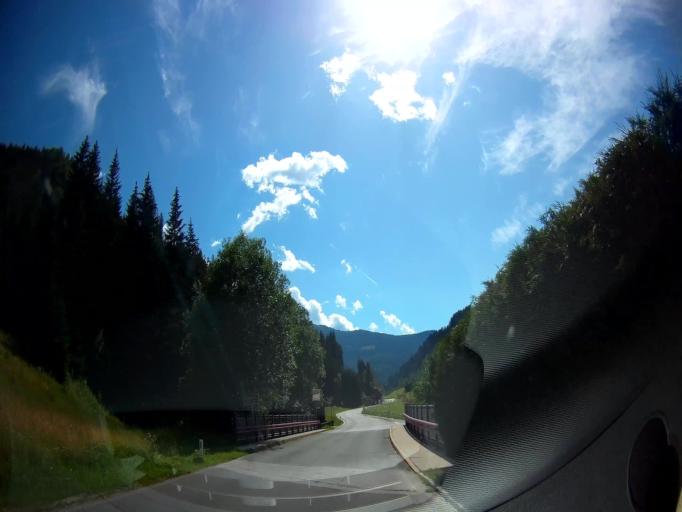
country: AT
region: Salzburg
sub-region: Politischer Bezirk Tamsweg
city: Ramingstein
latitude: 47.0751
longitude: 13.8108
